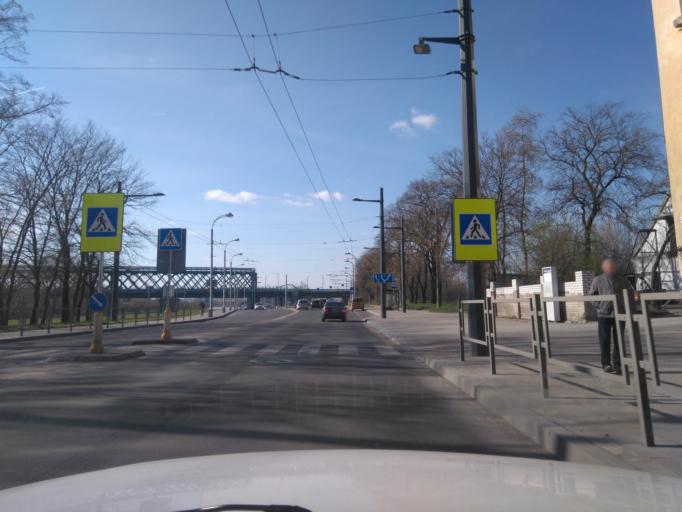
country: LT
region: Kauno apskritis
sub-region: Kaunas
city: Aleksotas
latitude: 54.8813
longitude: 23.9288
